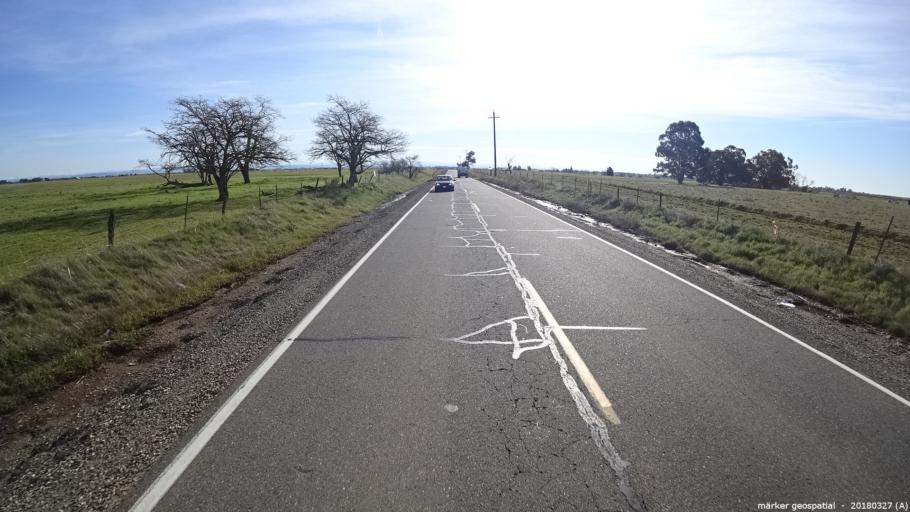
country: US
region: California
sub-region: Sacramento County
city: Vineyard
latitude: 38.4961
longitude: -121.2774
